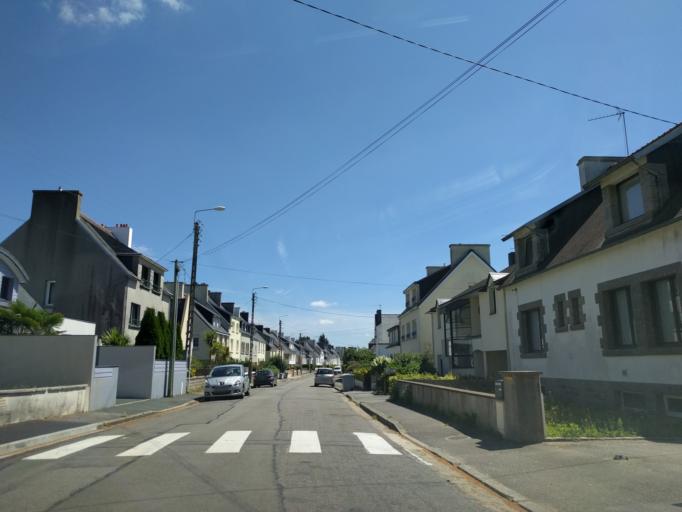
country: FR
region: Brittany
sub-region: Departement du Finistere
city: Quimper
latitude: 47.9890
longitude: -4.0985
